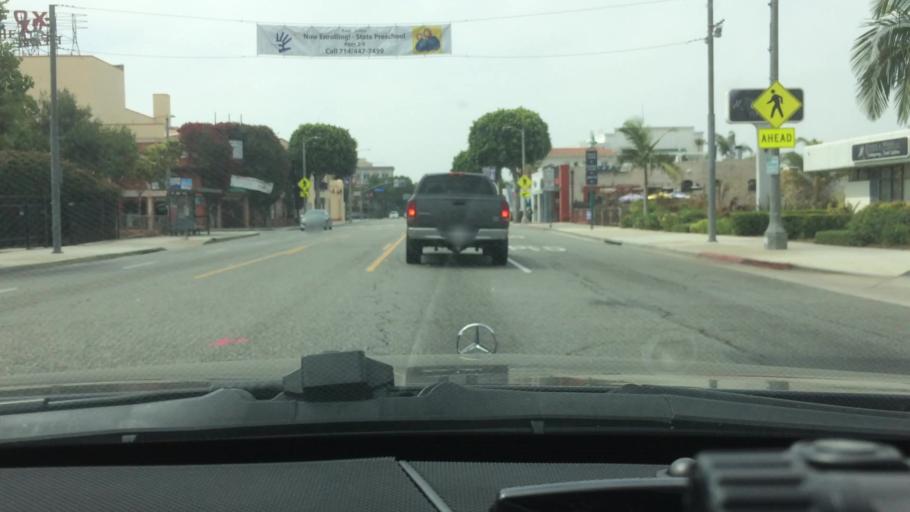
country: US
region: California
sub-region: Orange County
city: Fullerton
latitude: 33.8754
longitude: -117.9244
